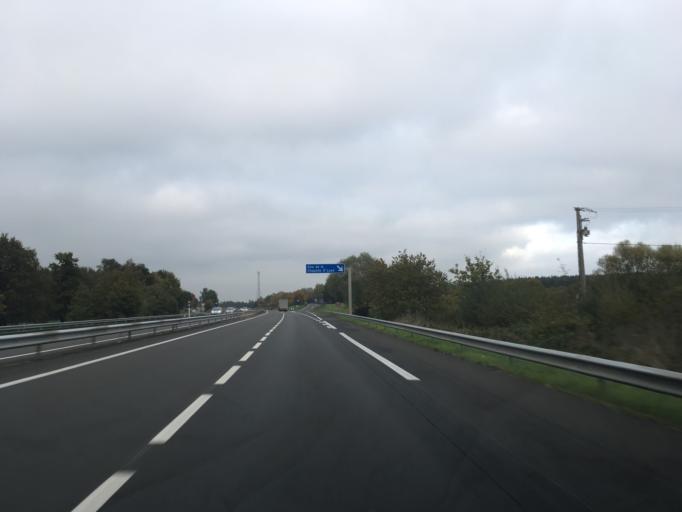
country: FR
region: Pays de la Loire
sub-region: Departement de Maine-et-Loire
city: Durtal
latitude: 47.6202
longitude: -0.2846
